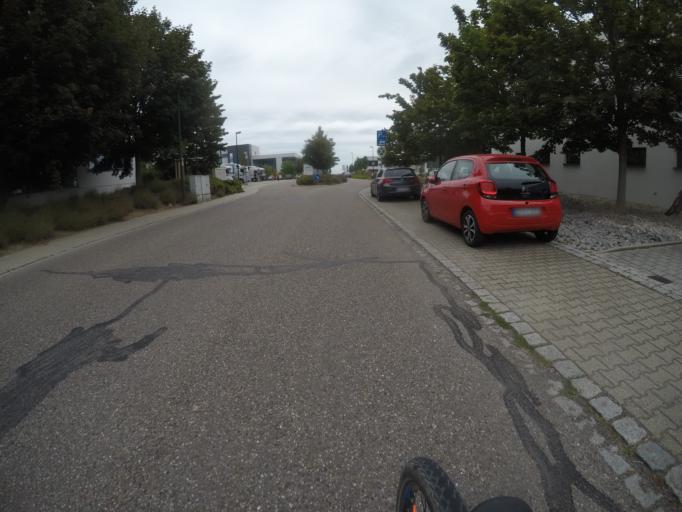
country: DE
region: Baden-Wuerttemberg
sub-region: Karlsruhe Region
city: Illingen
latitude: 48.9516
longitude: 8.8837
